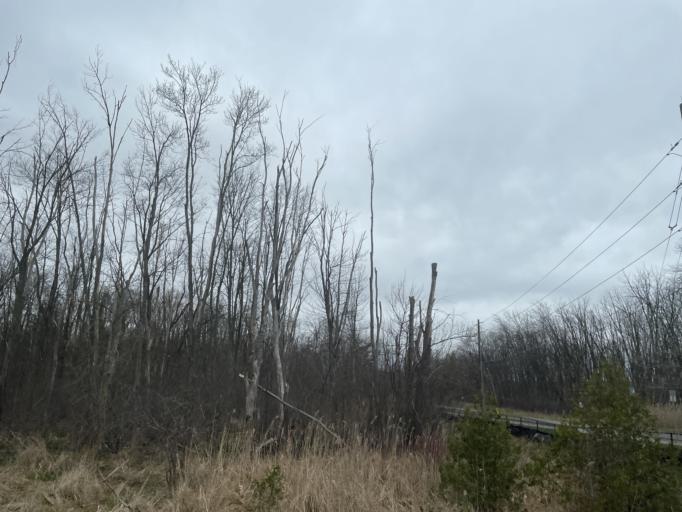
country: CA
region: Ontario
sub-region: Wellington County
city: Guelph
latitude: 43.5778
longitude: -80.2240
